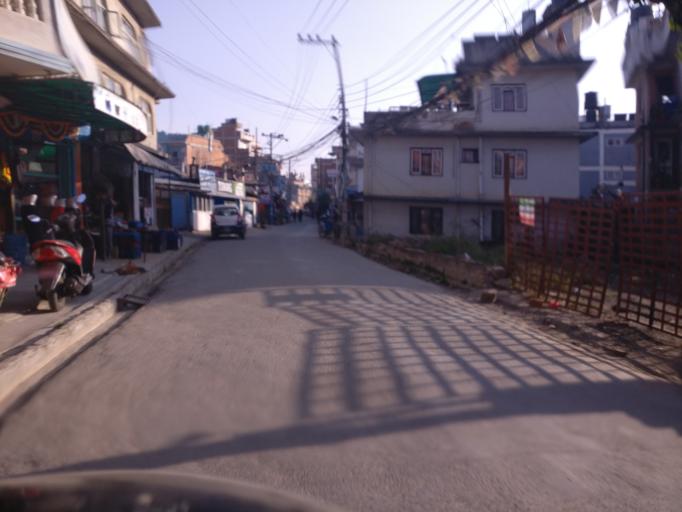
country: NP
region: Central Region
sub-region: Bagmati Zone
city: Patan
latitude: 27.6570
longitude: 85.3196
